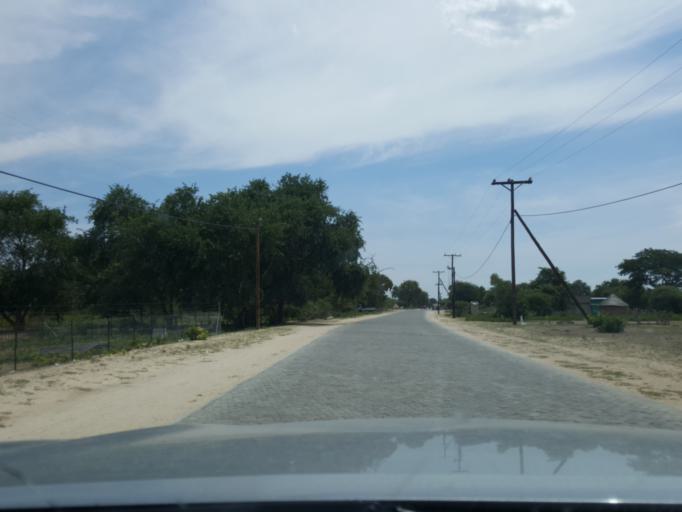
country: BW
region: North West
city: Shakawe
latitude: -18.3830
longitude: 21.8447
